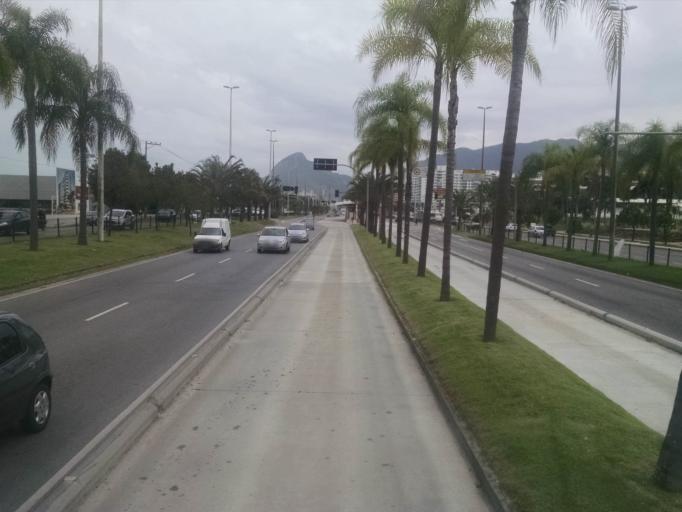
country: BR
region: Rio de Janeiro
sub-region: Sao Joao De Meriti
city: Sao Joao de Meriti
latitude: -22.9734
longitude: -43.3748
